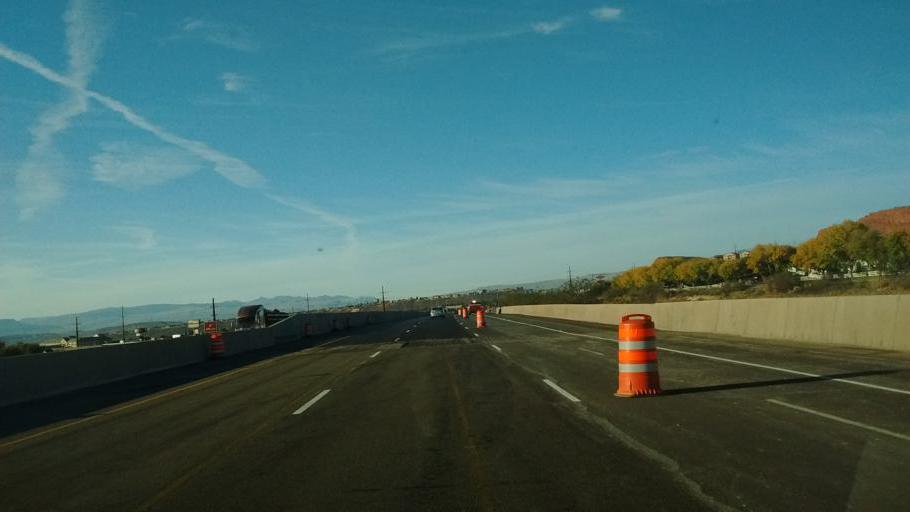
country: US
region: Utah
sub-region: Washington County
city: Washington
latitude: 37.1287
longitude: -113.5253
